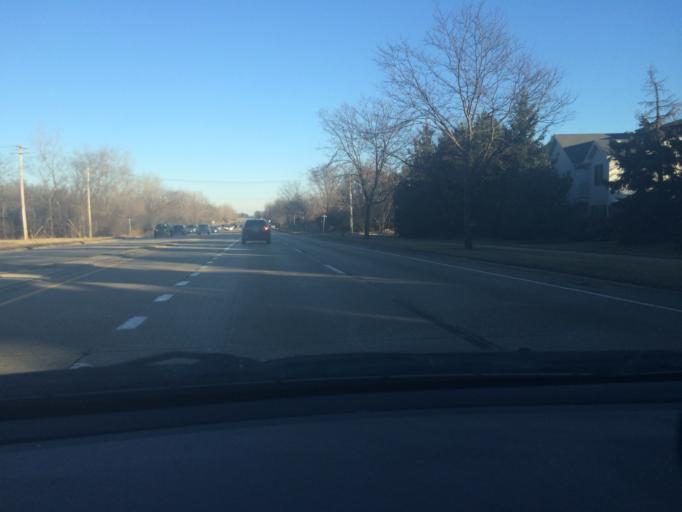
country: US
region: Illinois
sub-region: Lake County
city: Long Grove
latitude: 42.1536
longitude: -88.0007
